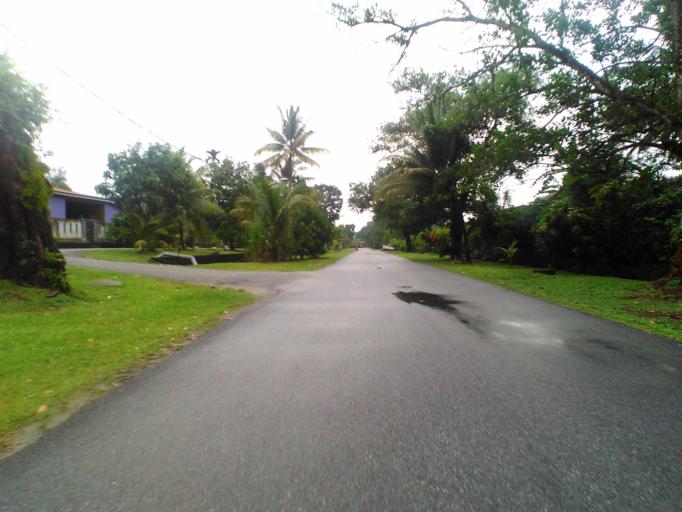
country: MY
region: Kedah
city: Kulim
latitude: 5.3619
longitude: 100.5766
